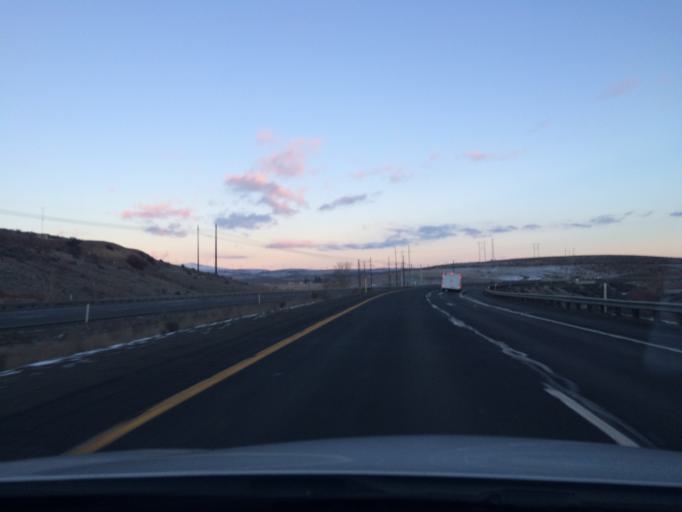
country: US
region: Washington
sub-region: Kittitas County
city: Kittitas
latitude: 46.9564
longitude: -120.3028
